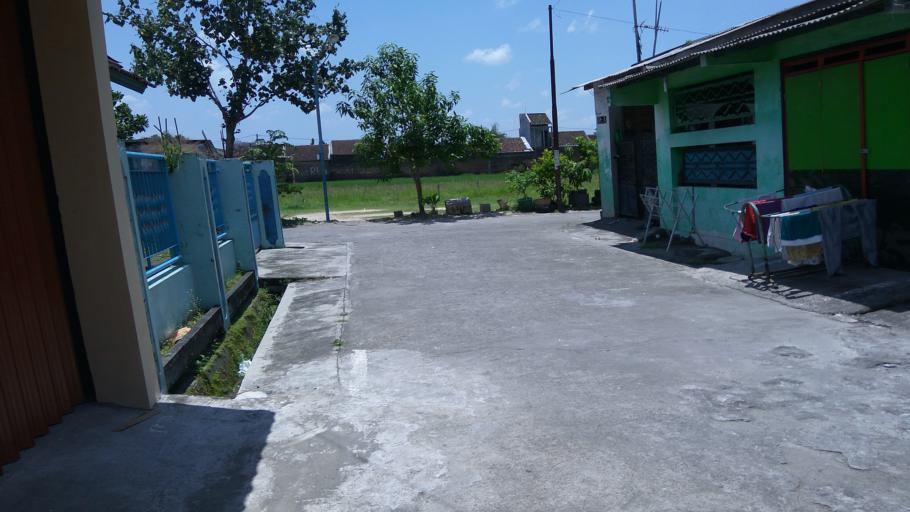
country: ID
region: Central Java
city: Grogol
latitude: -7.5917
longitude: 110.8025
